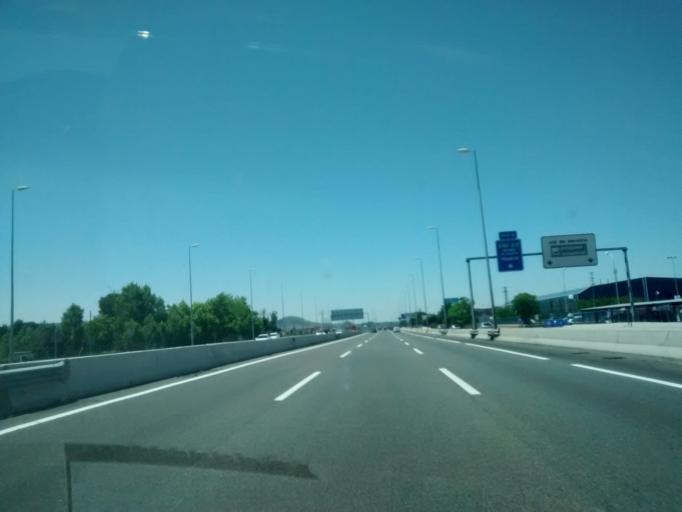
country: ES
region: Castille-La Mancha
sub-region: Provincia de Guadalajara
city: Azuqueca de Henares
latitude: 40.5532
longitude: -3.2650
